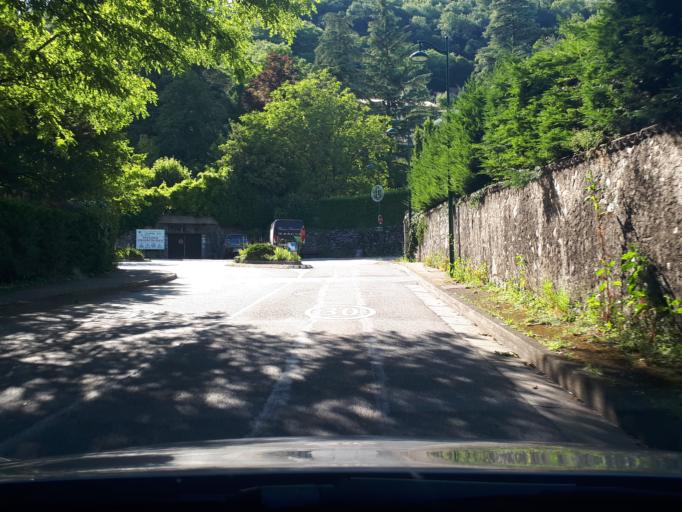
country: FR
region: Rhone-Alpes
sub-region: Departement de l'Isere
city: Seyssinet-Pariset
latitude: 45.1713
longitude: 5.6816
